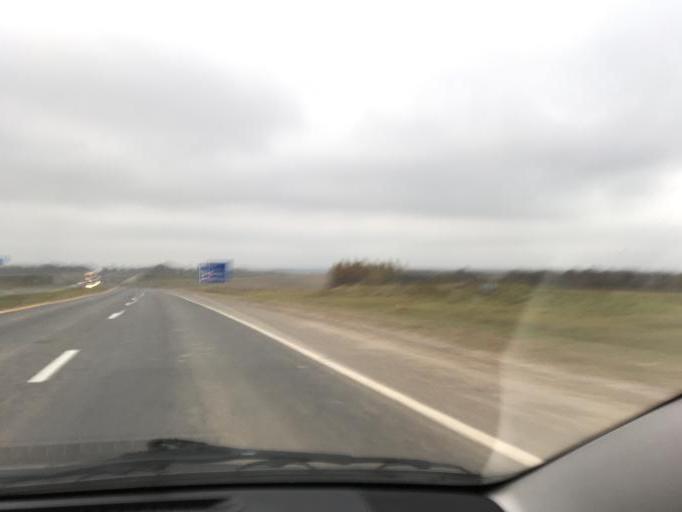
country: BY
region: Vitebsk
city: Vitebsk
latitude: 55.1559
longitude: 30.0769
